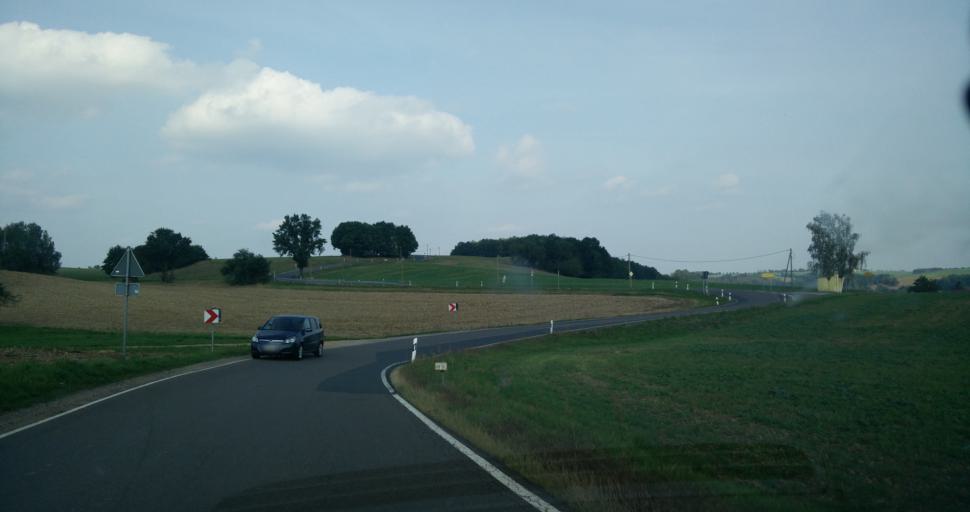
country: DE
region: Saxony
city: Rochlitz
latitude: 51.0798
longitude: 12.7912
